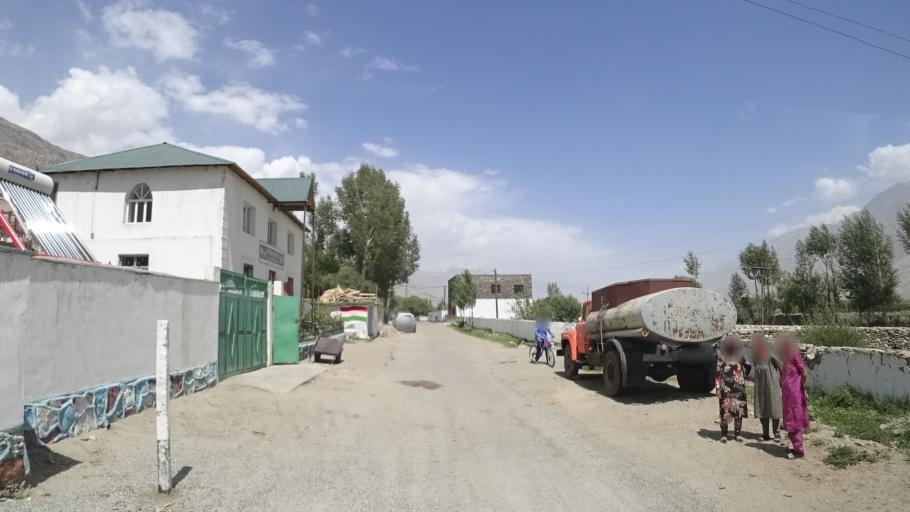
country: AF
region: Badakhshan
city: Khandud
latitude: 36.9203
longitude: 72.1910
